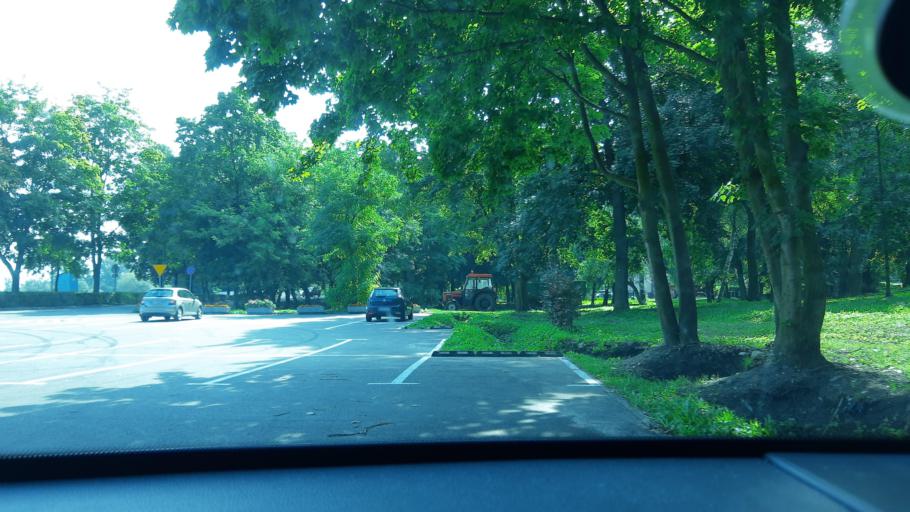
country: PL
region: Lodz Voivodeship
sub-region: Powiat sieradzki
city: Sieradz
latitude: 51.5997
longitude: 18.7403
